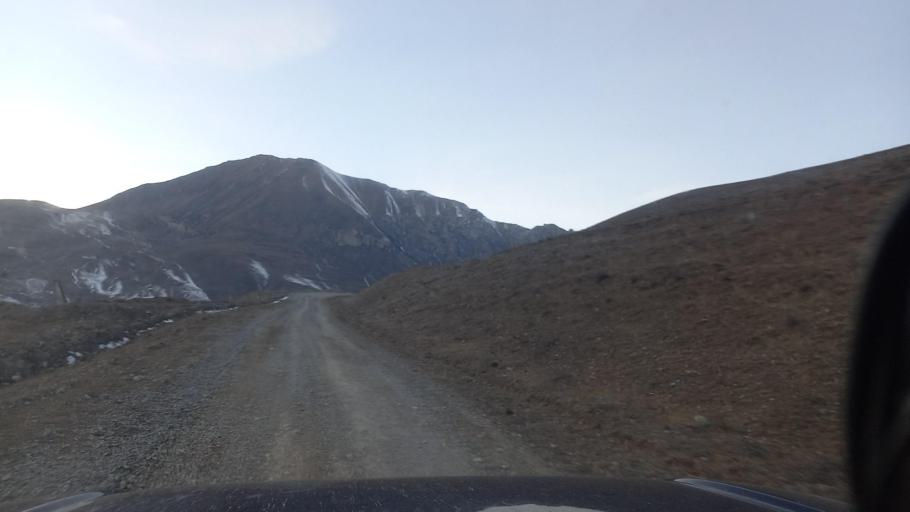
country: RU
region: Ingushetiya
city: Dzhayrakh
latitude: 42.8392
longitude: 44.5419
